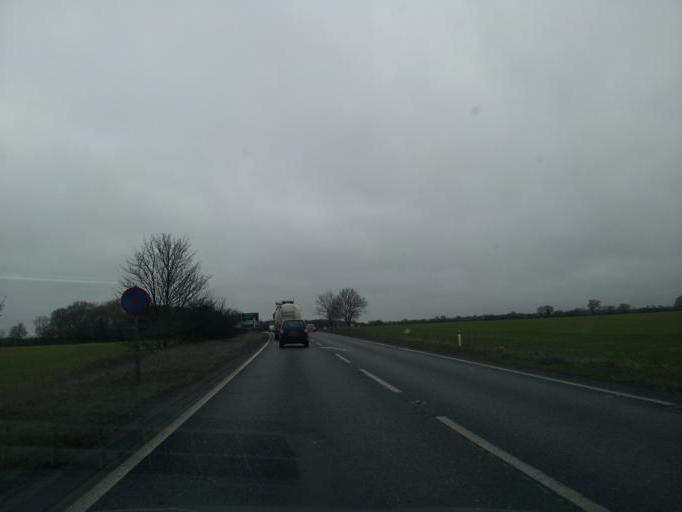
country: GB
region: England
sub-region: Essex
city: Great Bentley
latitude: 51.8921
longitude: 1.0646
